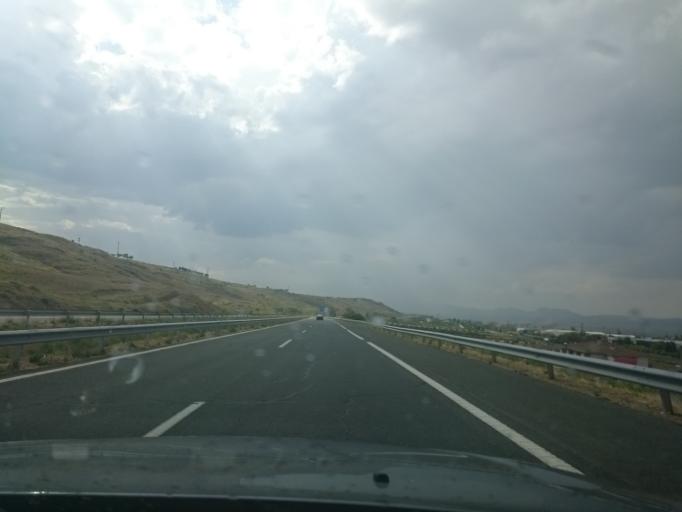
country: ES
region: La Rioja
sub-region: Provincia de La Rioja
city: Agoncillo
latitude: 42.4302
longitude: -2.2800
